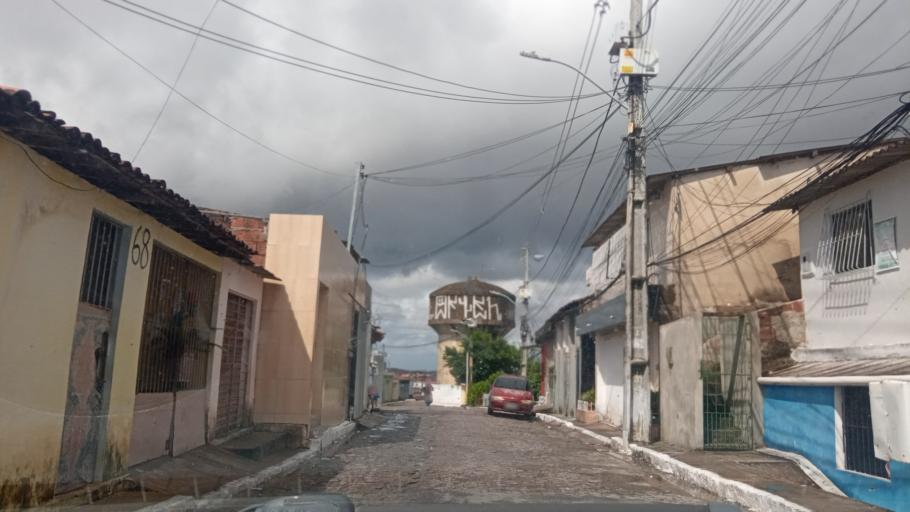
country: BR
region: Pernambuco
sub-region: Jaboatao Dos Guararapes
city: Jaboatao dos Guararapes
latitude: -8.1324
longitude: -34.9538
